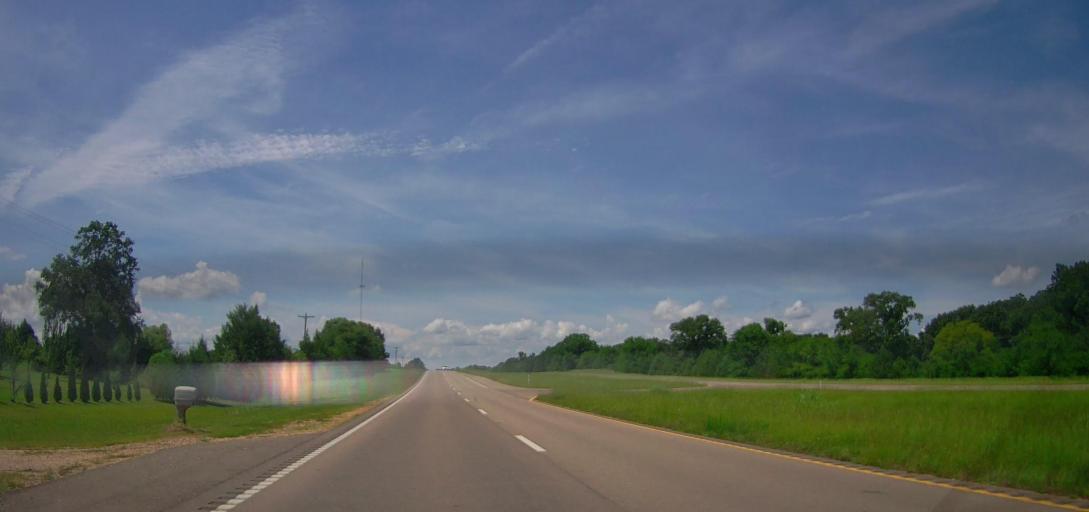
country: US
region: Mississippi
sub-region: Monroe County
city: Amory
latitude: 33.9465
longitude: -88.6014
